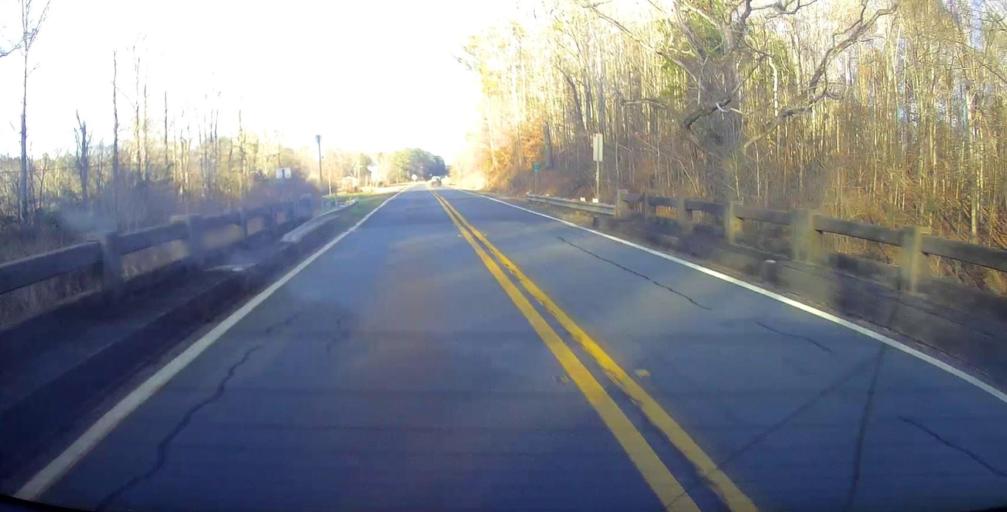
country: US
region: Georgia
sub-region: Talbot County
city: Talbotton
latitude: 32.7994
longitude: -84.5030
